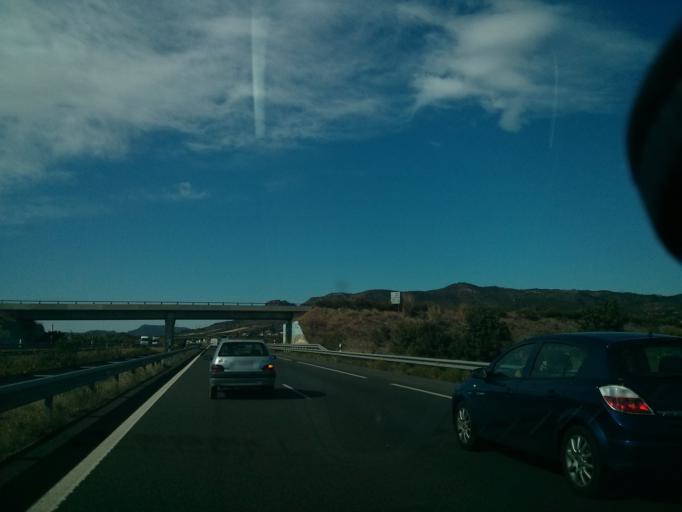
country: ES
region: Valencia
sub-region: Provincia de Valencia
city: Benavites
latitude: 39.7300
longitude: -0.2436
